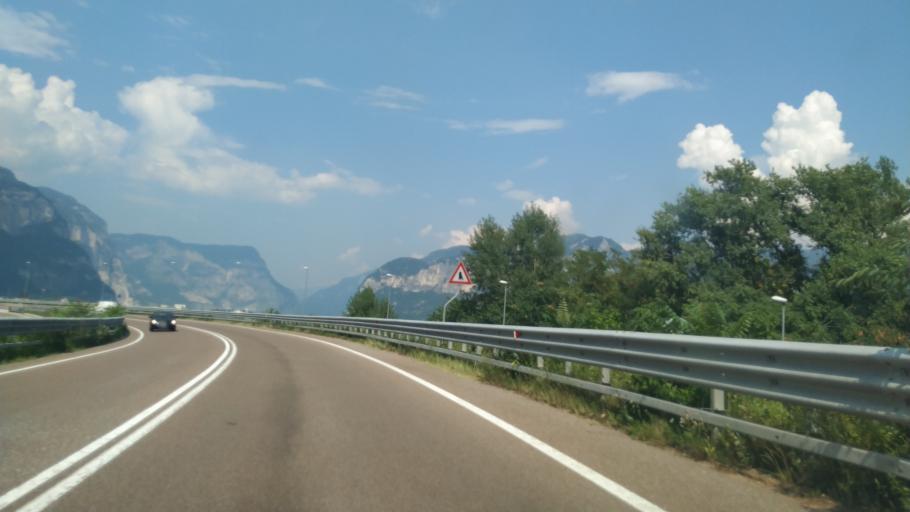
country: IT
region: Trentino-Alto Adige
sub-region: Provincia di Trento
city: Mezzolombardo
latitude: 46.1881
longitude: 11.1011
